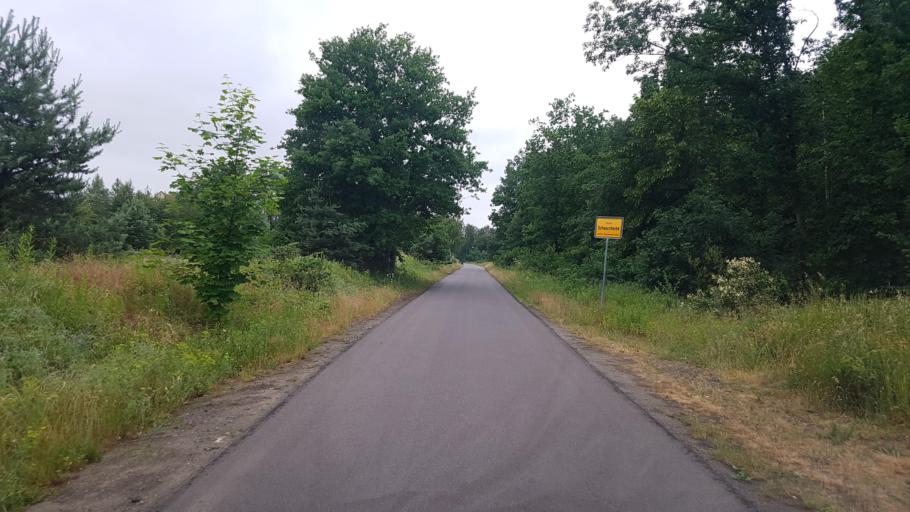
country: DE
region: Brandenburg
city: Schwarzbach
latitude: 51.4808
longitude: 13.9137
